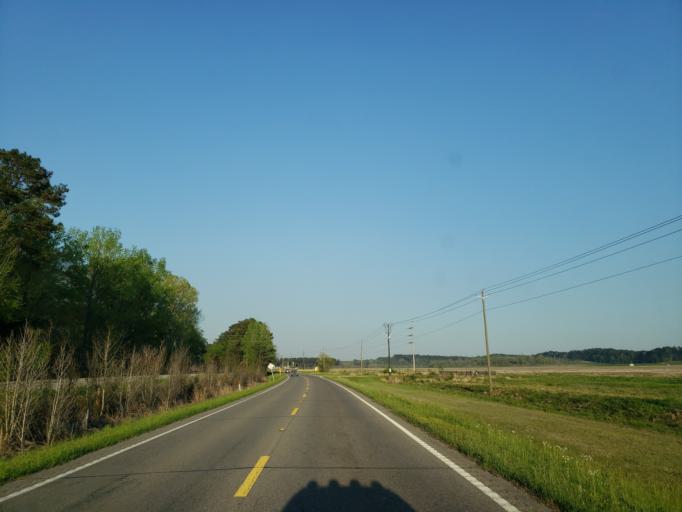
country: US
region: Mississippi
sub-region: Lauderdale County
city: Marion
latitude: 32.3941
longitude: -88.6301
